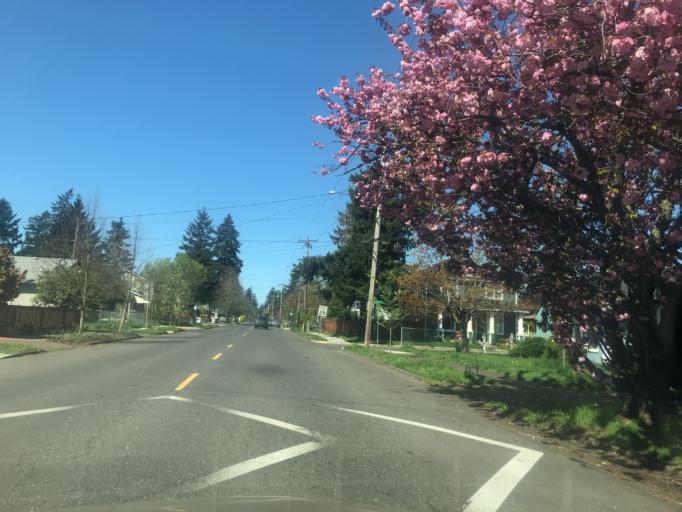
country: US
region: Oregon
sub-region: Multnomah County
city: Lents
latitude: 45.4831
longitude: -122.5963
